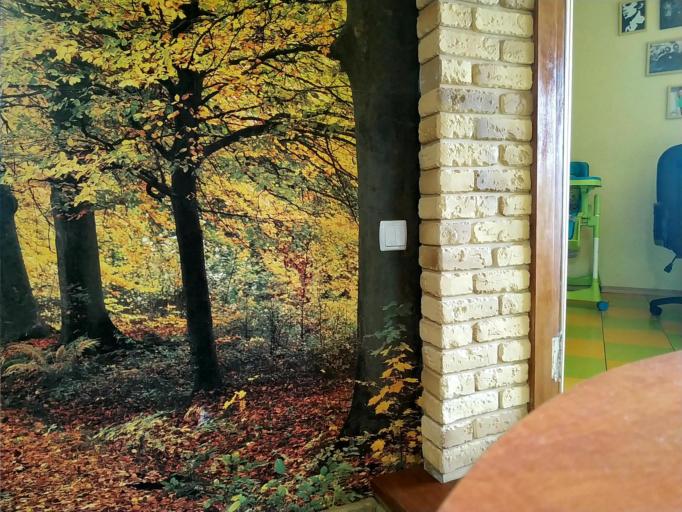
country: RU
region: Smolensk
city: Ozernyy
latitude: 55.4665
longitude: 32.6662
